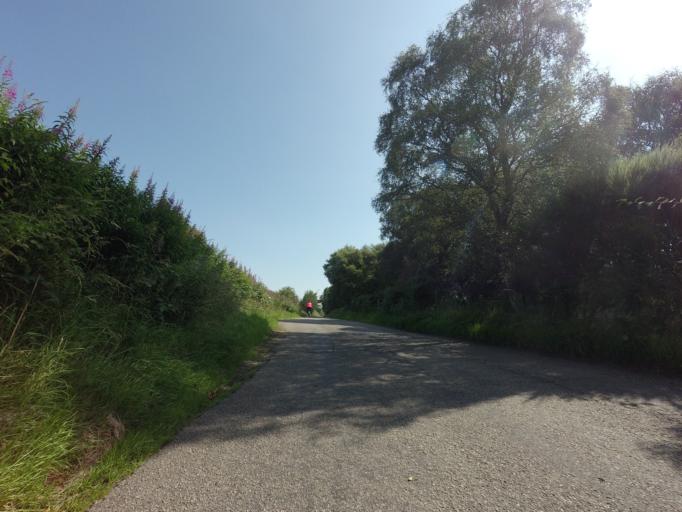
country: GB
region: Scotland
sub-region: Highland
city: Invergordon
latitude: 57.7551
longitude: -4.1404
